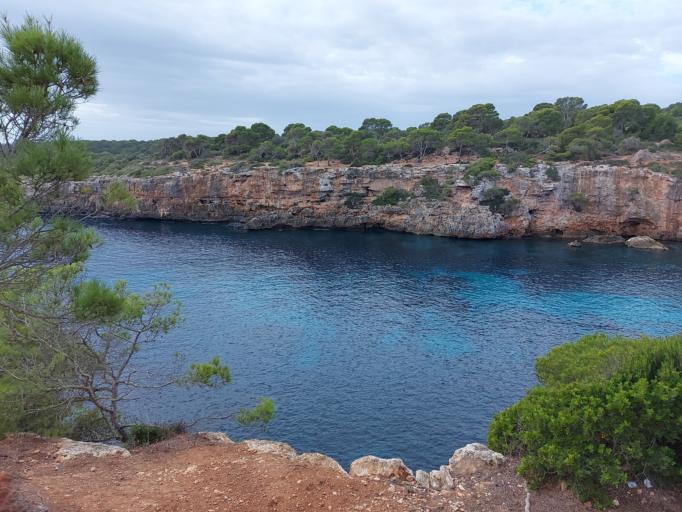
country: ES
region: Balearic Islands
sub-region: Illes Balears
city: Llucmajor
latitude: 39.3617
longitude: 2.8351
